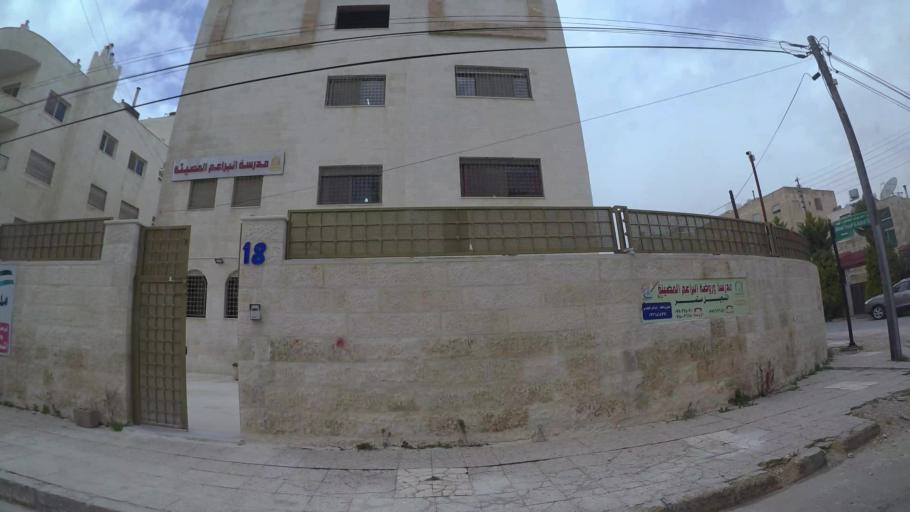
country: JO
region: Amman
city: Umm as Summaq
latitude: 31.8944
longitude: 35.8436
